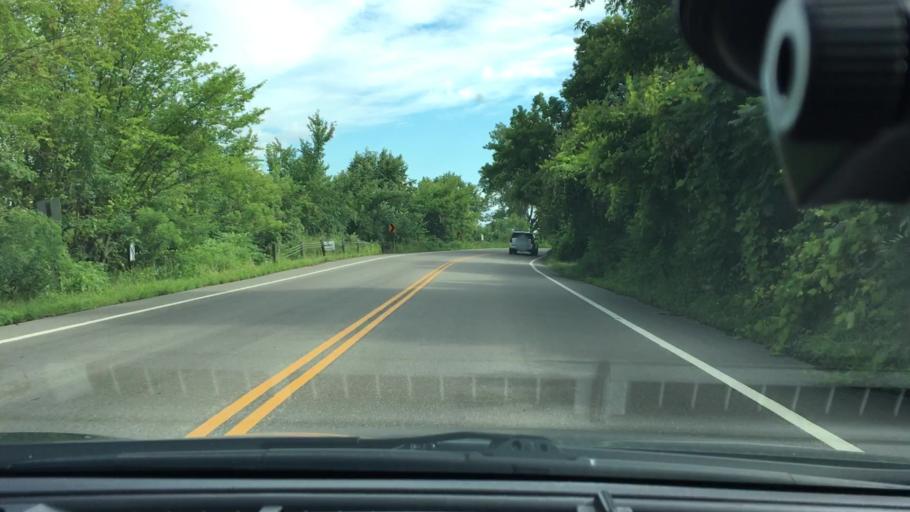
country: US
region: Minnesota
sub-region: Hennepin County
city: Orono
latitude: 44.9485
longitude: -93.5762
